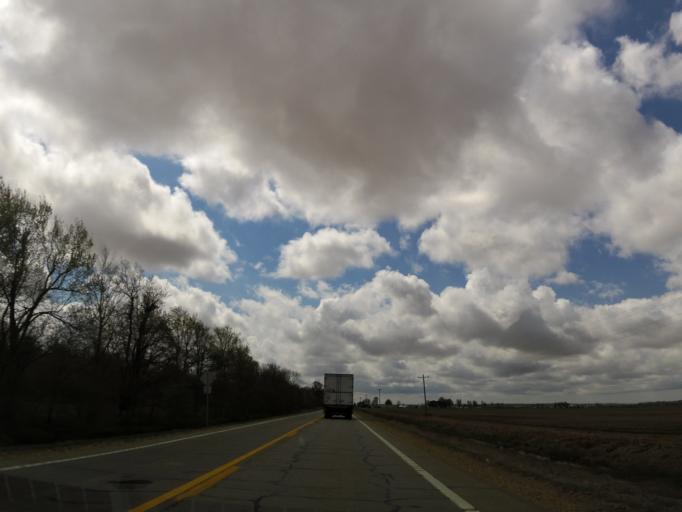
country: US
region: Arkansas
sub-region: Clay County
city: Corning
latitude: 36.2914
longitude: -90.5346
